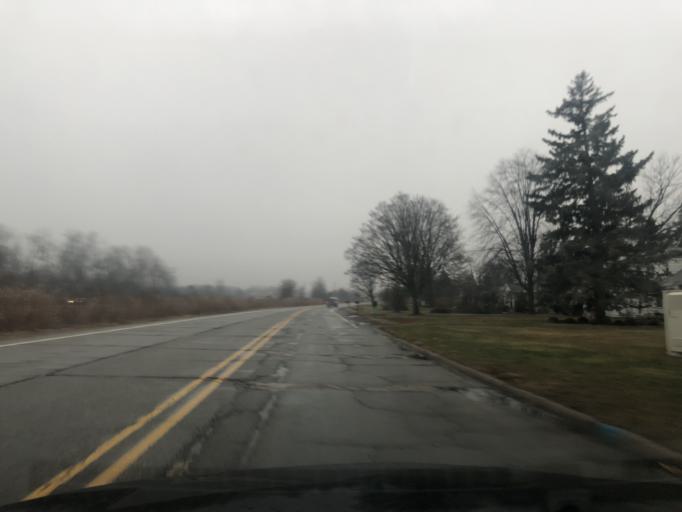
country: US
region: Michigan
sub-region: Wayne County
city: Rockwood
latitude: 42.0987
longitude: -83.2260
